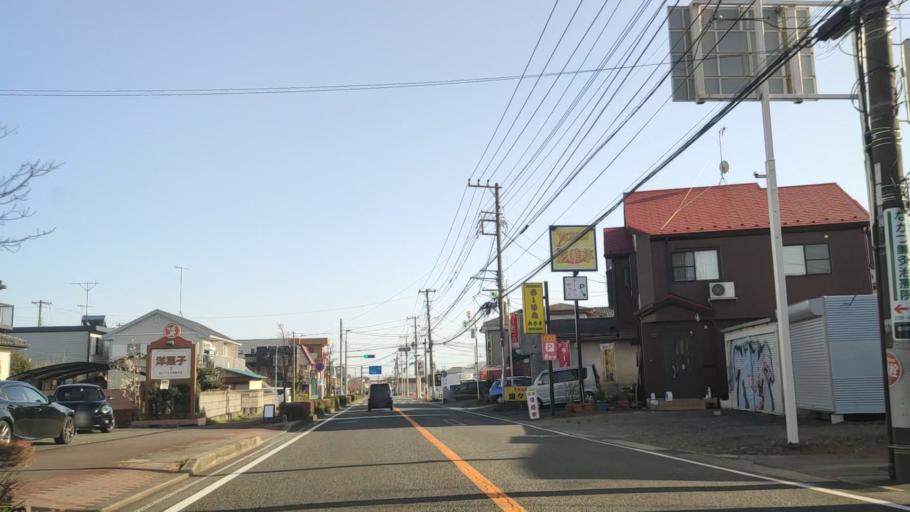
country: JP
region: Kanagawa
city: Zama
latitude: 35.5086
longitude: 139.3394
